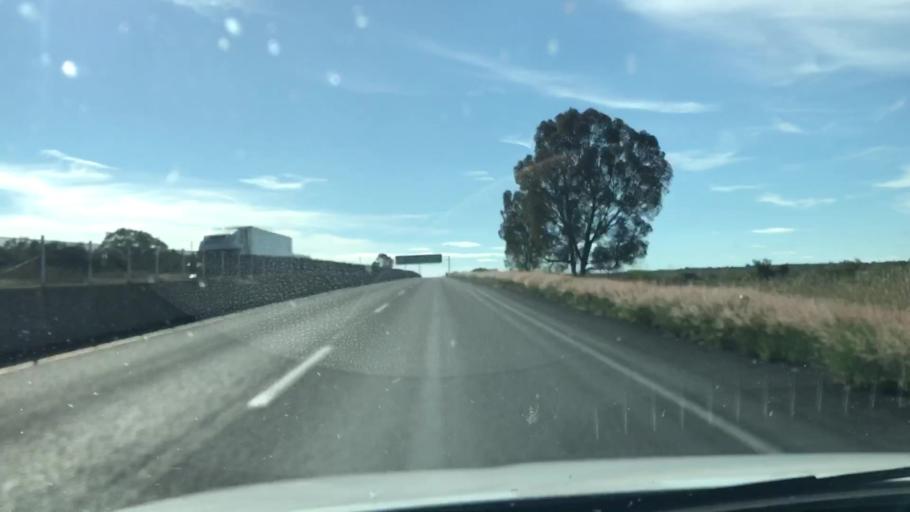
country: MX
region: Guanajuato
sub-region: Leon
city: Rizos de la Joya (Rizos del Saucillo)
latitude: 21.1211
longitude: -101.8089
